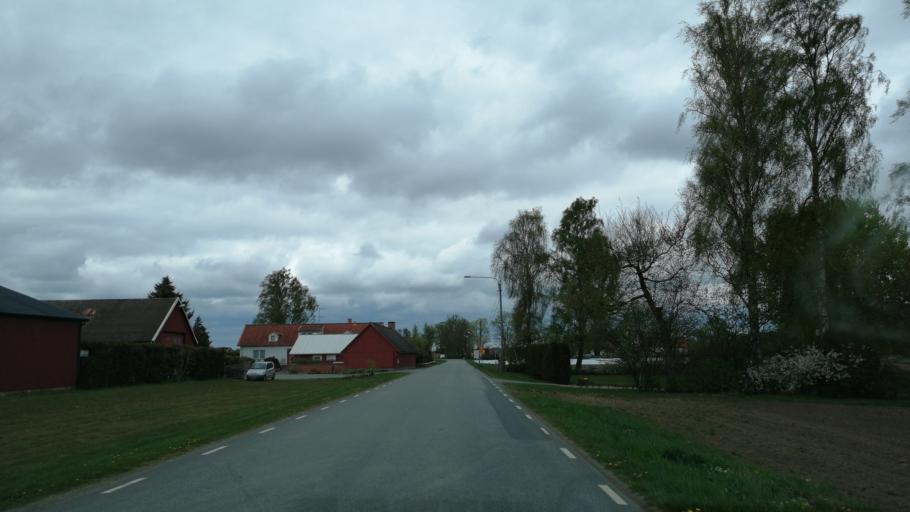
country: SE
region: Skane
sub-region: Kristianstads Kommun
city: Fjalkinge
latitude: 56.0633
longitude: 14.3323
